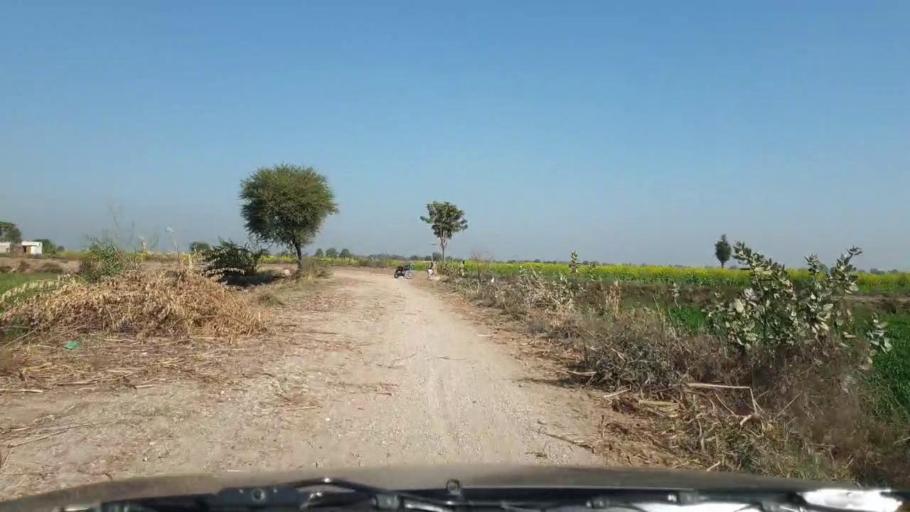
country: PK
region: Sindh
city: Jhol
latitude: 25.9633
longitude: 68.8236
